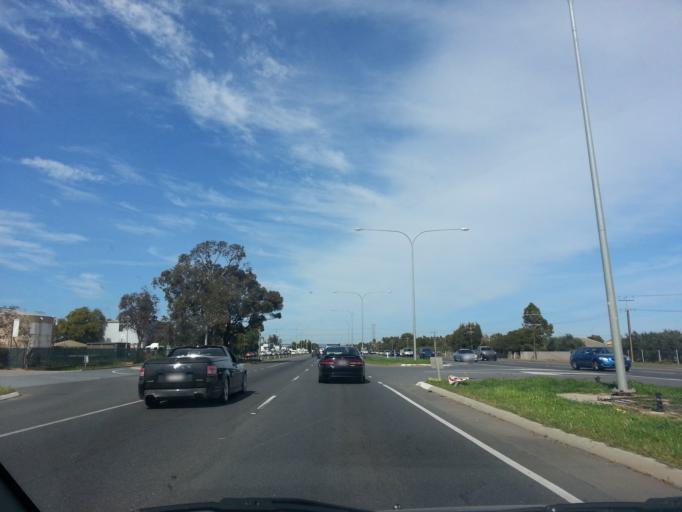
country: AU
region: South Australia
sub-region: Salisbury
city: Salisbury
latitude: -34.7804
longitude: 138.5955
